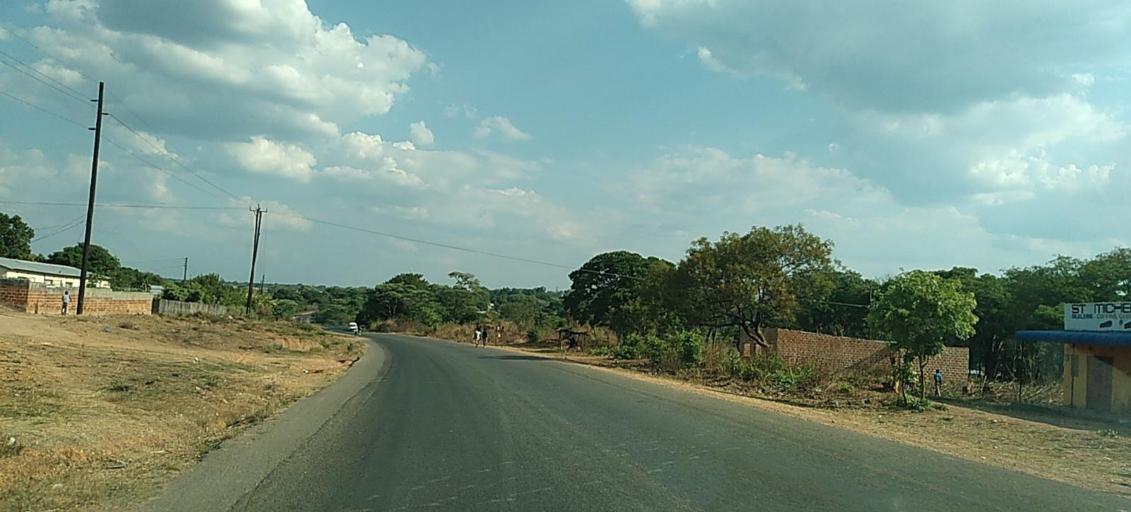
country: ZM
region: Copperbelt
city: Luanshya
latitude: -13.3429
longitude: 28.4182
